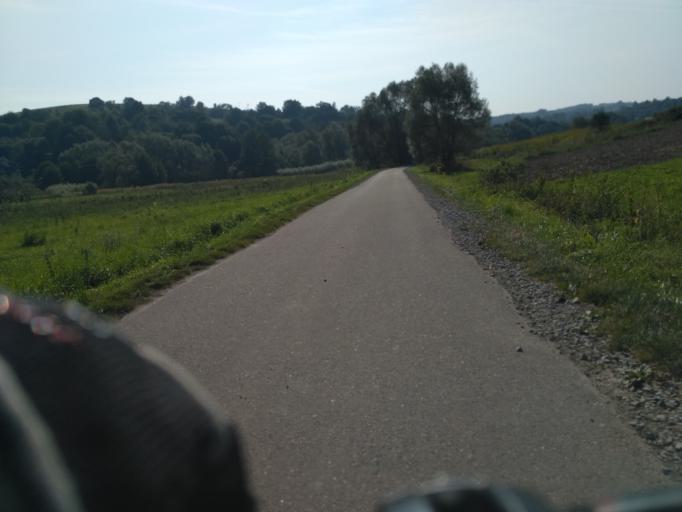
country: PL
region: Subcarpathian Voivodeship
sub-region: Powiat brzozowski
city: Golcowa
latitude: 49.7798
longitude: 22.0135
